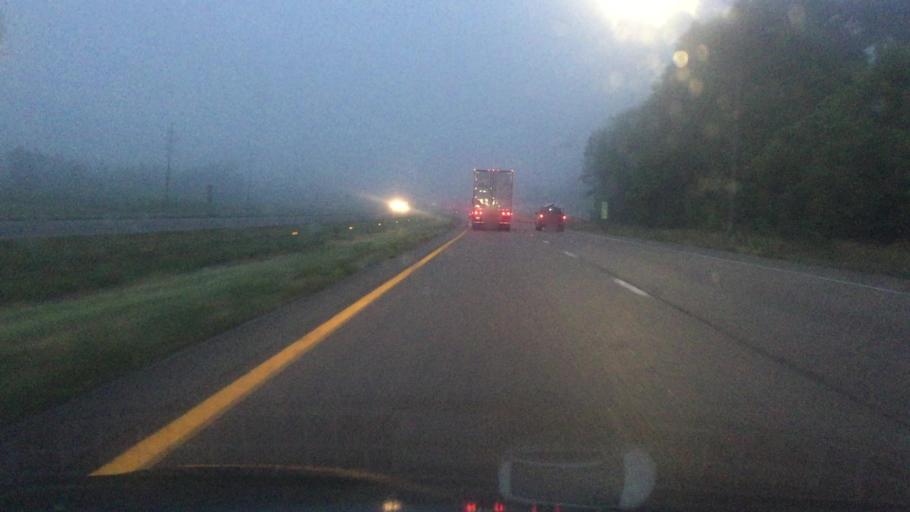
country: US
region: Missouri
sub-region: Montgomery County
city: Montgomery City
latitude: 38.8756
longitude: -91.3780
